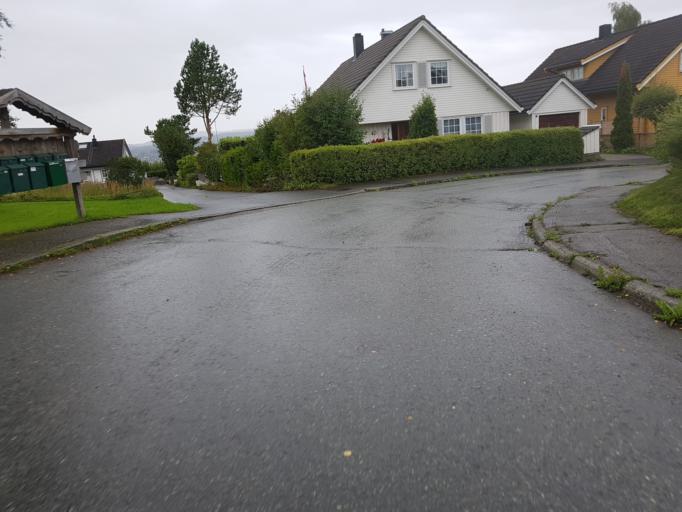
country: NO
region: Sor-Trondelag
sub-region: Trondheim
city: Trondheim
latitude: 63.4020
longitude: 10.4489
